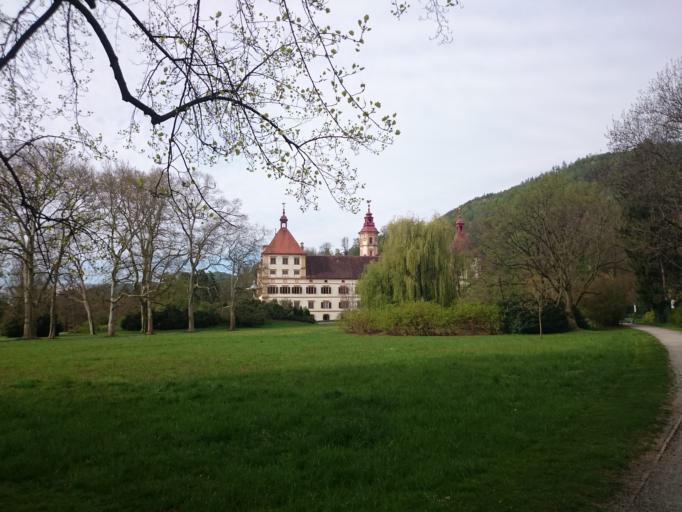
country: AT
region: Styria
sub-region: Graz Stadt
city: Goesting
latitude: 47.0754
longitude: 15.3932
